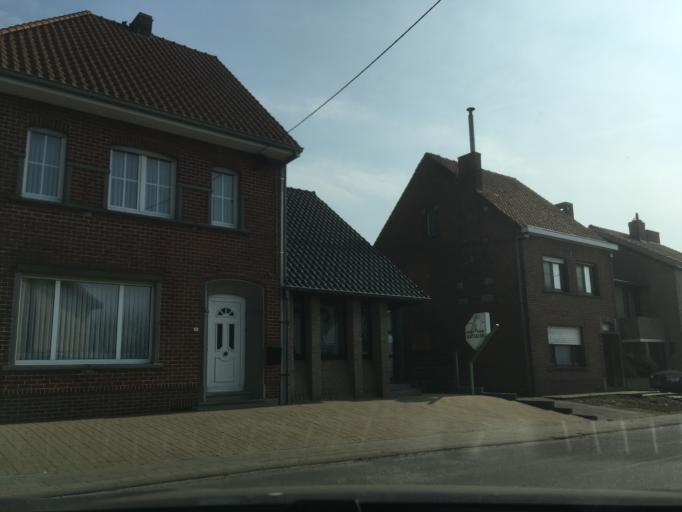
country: BE
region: Flanders
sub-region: Provincie West-Vlaanderen
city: Ardooie
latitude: 51.0326
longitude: 3.2083
